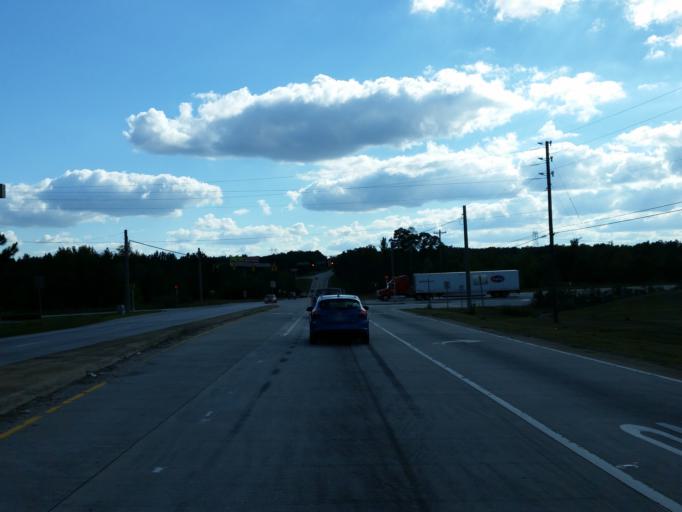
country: US
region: Georgia
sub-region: Butts County
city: Jackson
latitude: 33.2043
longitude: -84.0630
